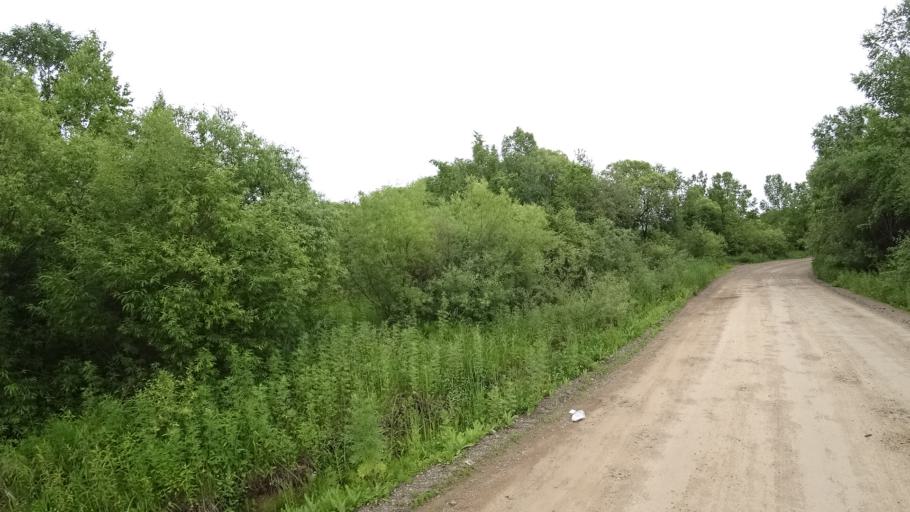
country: RU
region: Primorskiy
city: Arsen'yev
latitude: 44.1918
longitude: 133.3106
